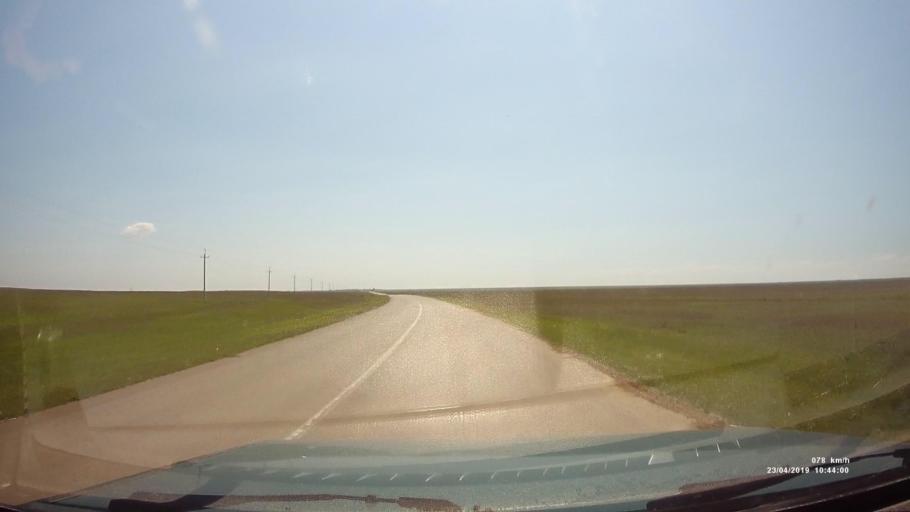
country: RU
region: Kalmykiya
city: Yashalta
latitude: 46.4633
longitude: 42.6511
